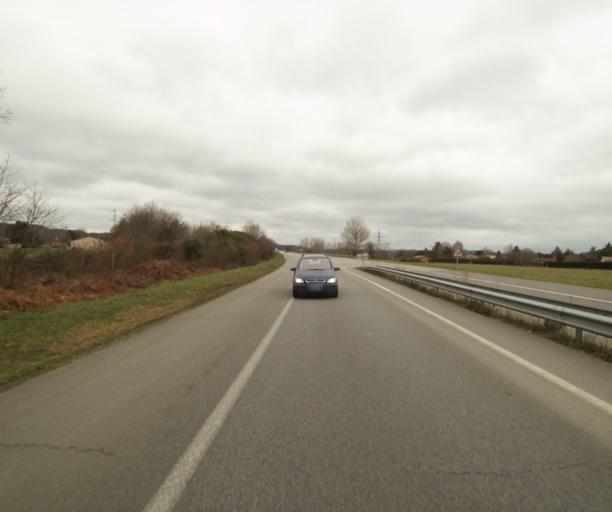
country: FR
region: Midi-Pyrenees
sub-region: Departement de l'Ariege
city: Pamiers
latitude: 43.1361
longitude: 1.6208
